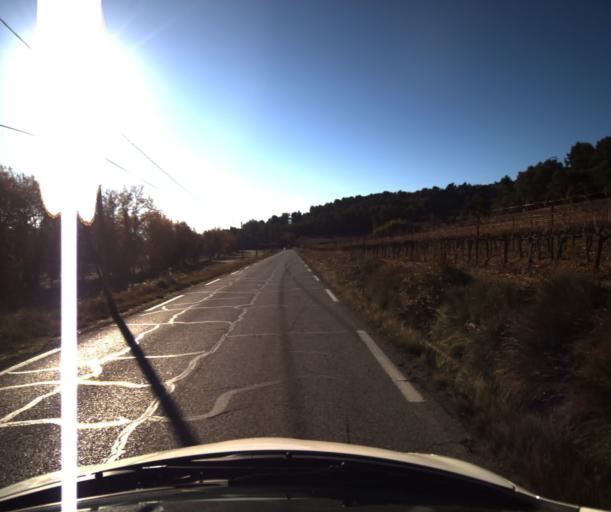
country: FR
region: Provence-Alpes-Cote d'Azur
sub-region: Departement du Vaucluse
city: Pertuis
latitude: 43.7210
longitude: 5.5043
